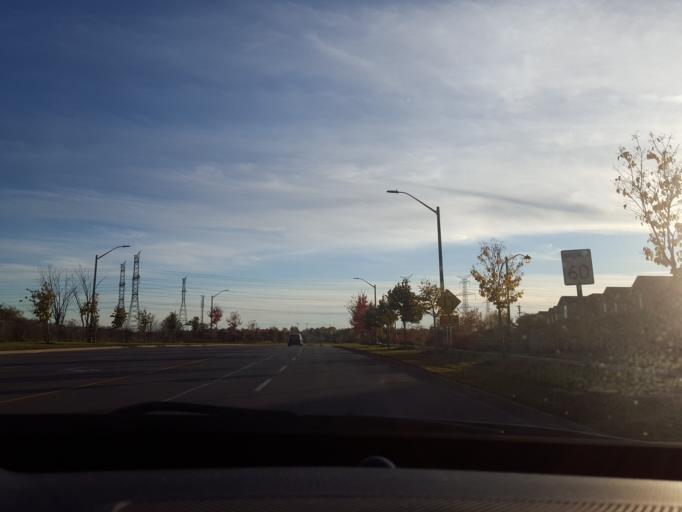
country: CA
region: Ontario
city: Markham
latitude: 43.8524
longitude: -79.2239
